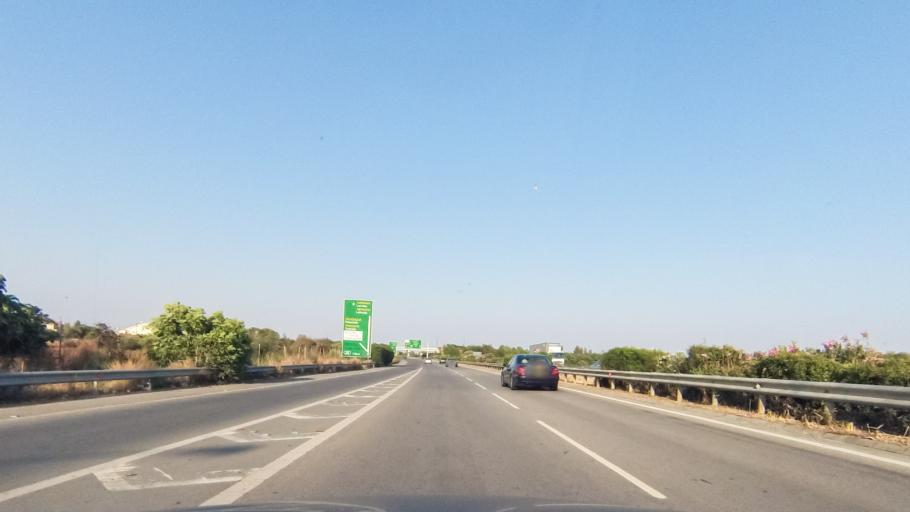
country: CY
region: Limassol
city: Pano Polemidia
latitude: 34.6873
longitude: 32.9930
